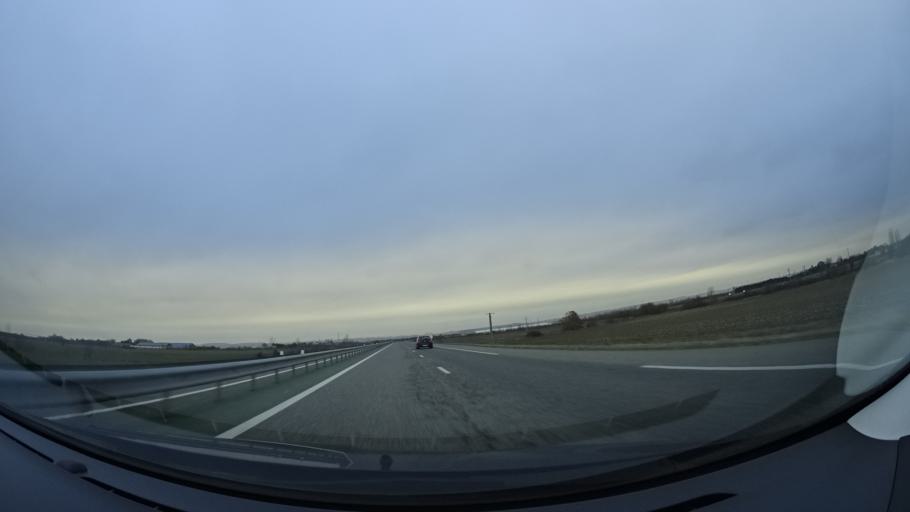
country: FR
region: Midi-Pyrenees
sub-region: Departement de l'Ariege
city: Mazeres
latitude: 43.2210
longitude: 1.6378
